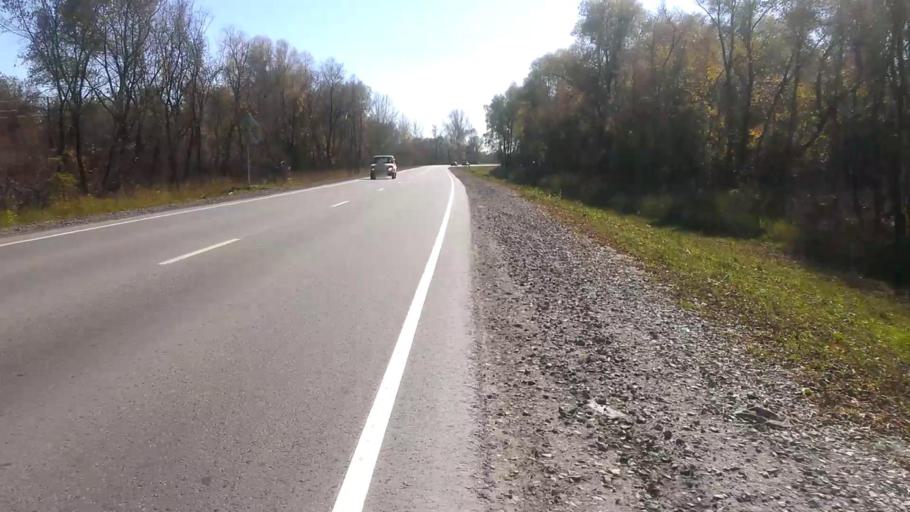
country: RU
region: Altai Krai
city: Sannikovo
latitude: 53.3256
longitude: 83.9421
